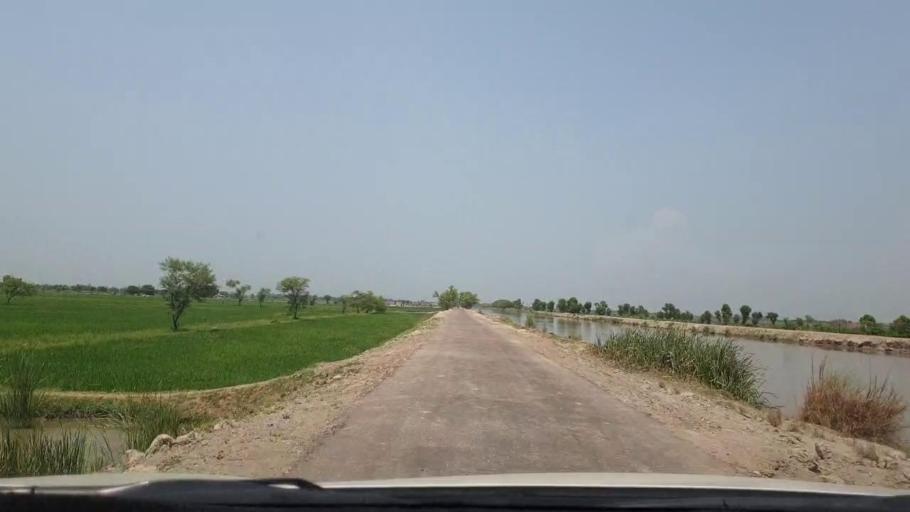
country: PK
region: Sindh
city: Dokri
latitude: 27.3402
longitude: 68.1108
